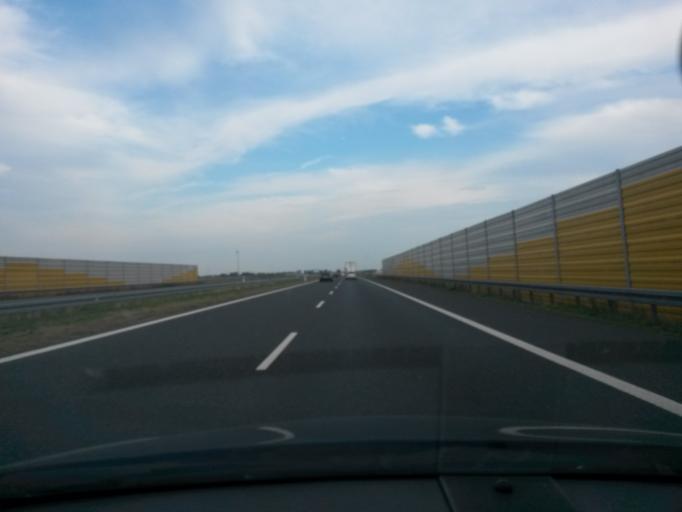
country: PL
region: Lodz Voivodeship
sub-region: Powiat leczycki
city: Swinice Warckie
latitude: 52.0179
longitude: 18.9404
